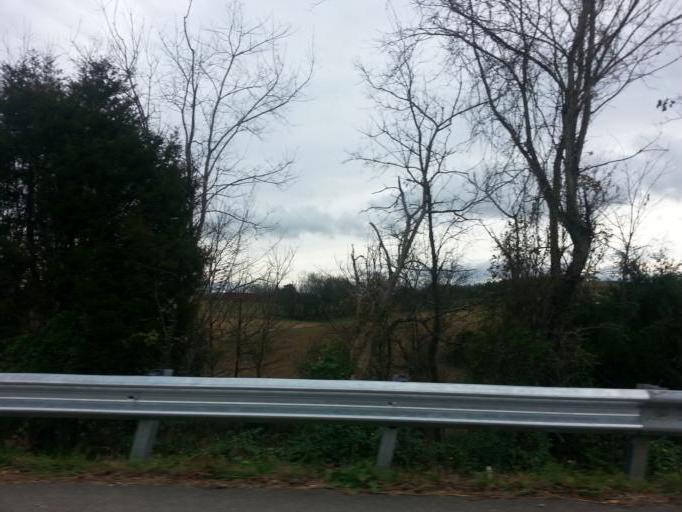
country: US
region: Tennessee
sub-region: Greene County
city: Mosheim
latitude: 36.0640
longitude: -82.9713
